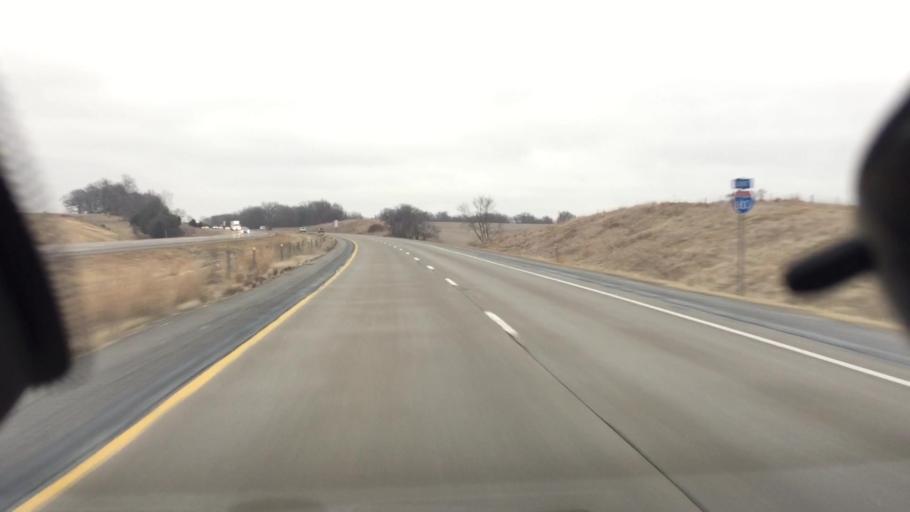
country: US
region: Iowa
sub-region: Johnson County
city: Iowa City
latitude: 41.6723
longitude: -91.4393
